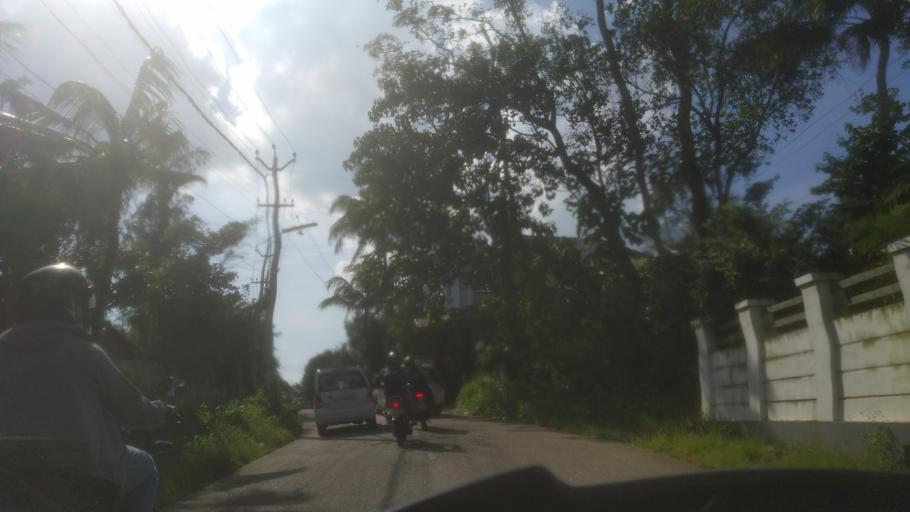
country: IN
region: Kerala
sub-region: Ernakulam
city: Muvattupula
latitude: 9.9977
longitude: 76.6181
